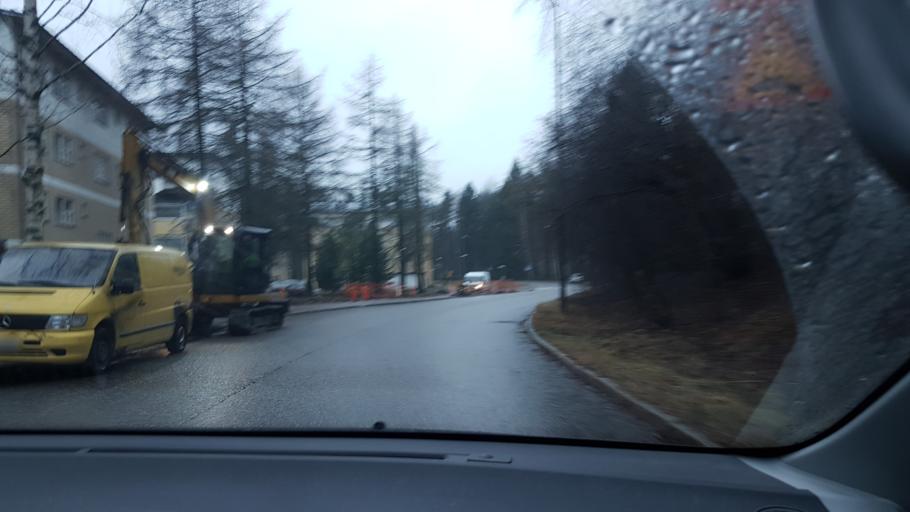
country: FI
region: Uusimaa
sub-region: Helsinki
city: Vantaa
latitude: 60.2331
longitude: 25.0724
